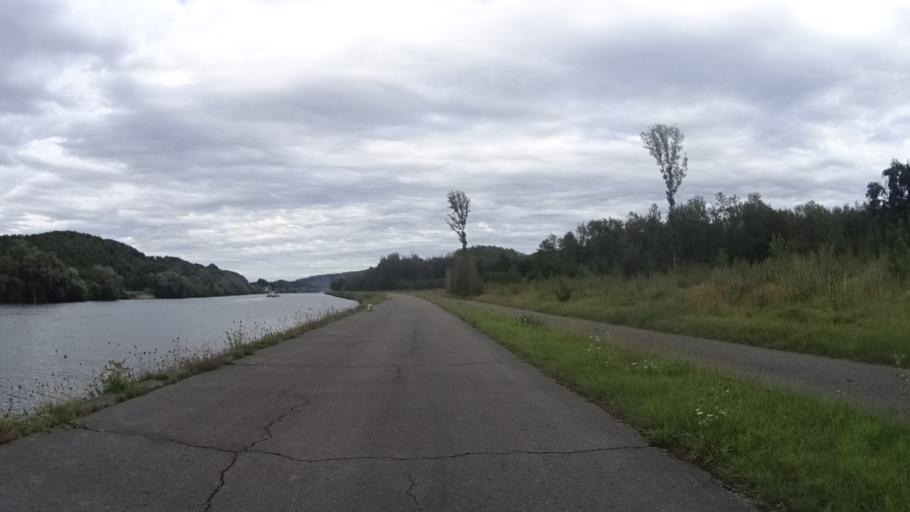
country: BE
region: Wallonia
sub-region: Province de Liege
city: Wanze
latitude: 50.5123
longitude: 5.1653
